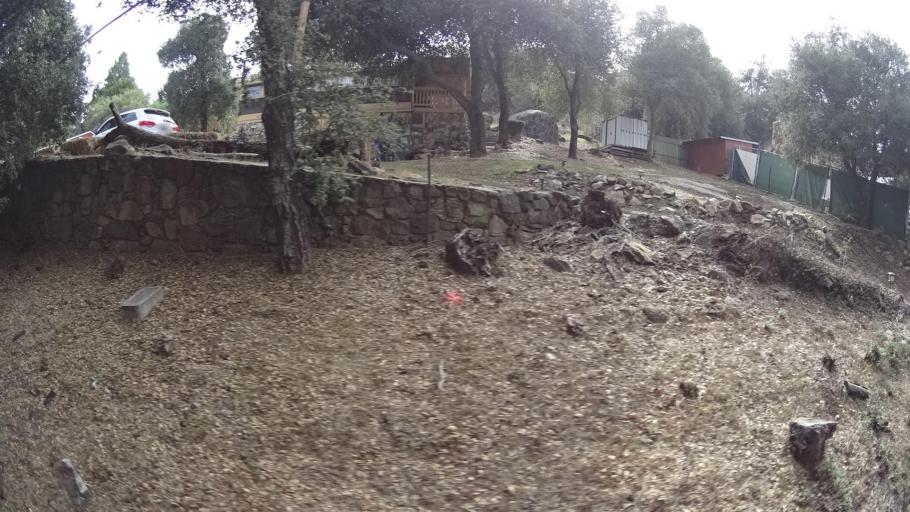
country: US
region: California
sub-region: San Diego County
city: Descanso
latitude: 32.8621
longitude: -116.6201
